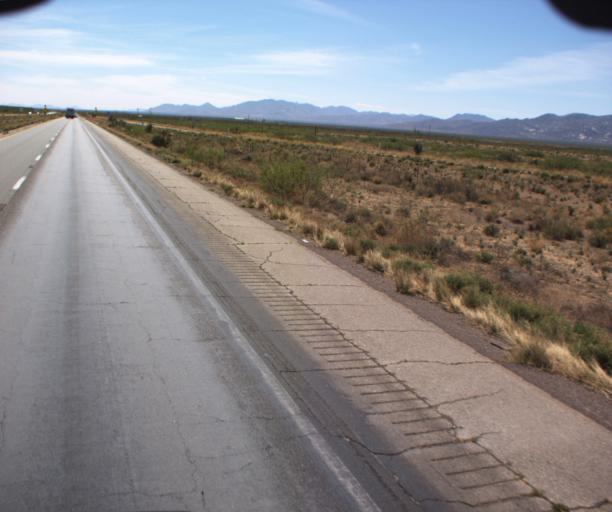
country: US
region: Arizona
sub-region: Cochise County
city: Willcox
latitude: 32.3289
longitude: -109.5124
